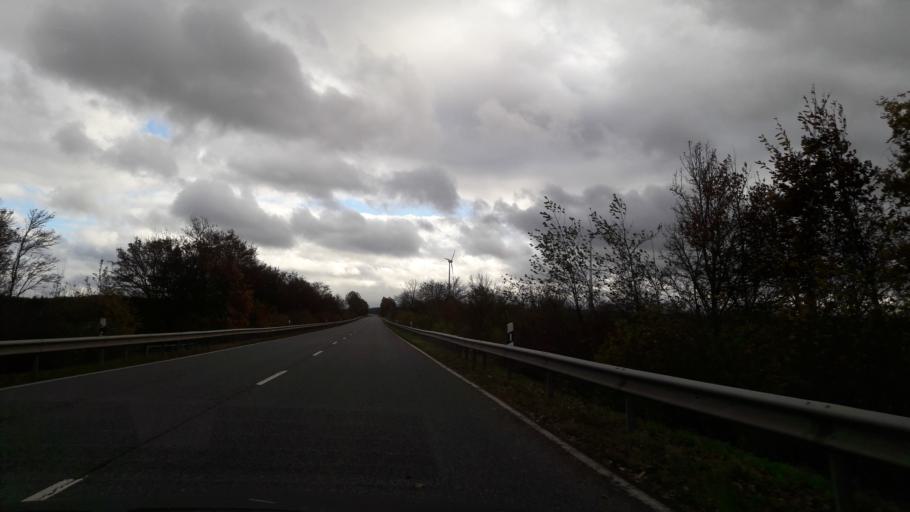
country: DE
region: Rheinland-Pfalz
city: Fell
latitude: 49.7515
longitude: 6.7766
